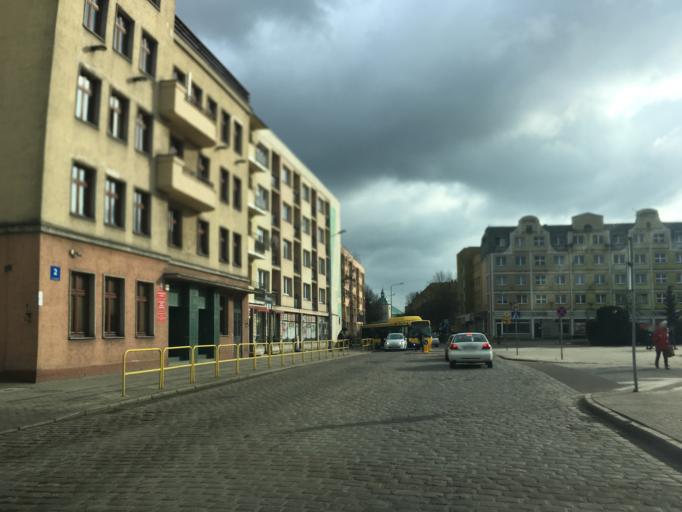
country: PL
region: Pomeranian Voivodeship
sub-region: Slupsk
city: Slupsk
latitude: 54.4672
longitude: 17.0315
